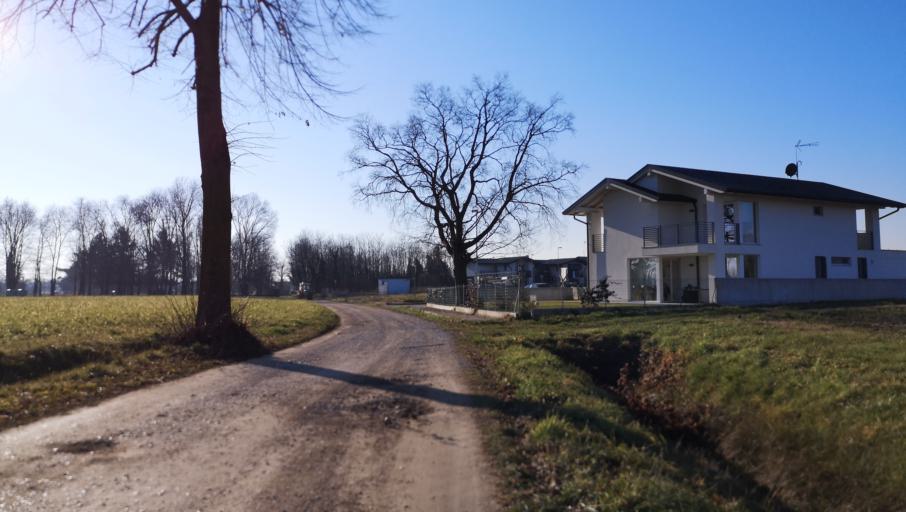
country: IT
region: Friuli Venezia Giulia
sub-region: Provincia di Udine
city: Palmanova
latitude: 45.9153
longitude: 13.2990
